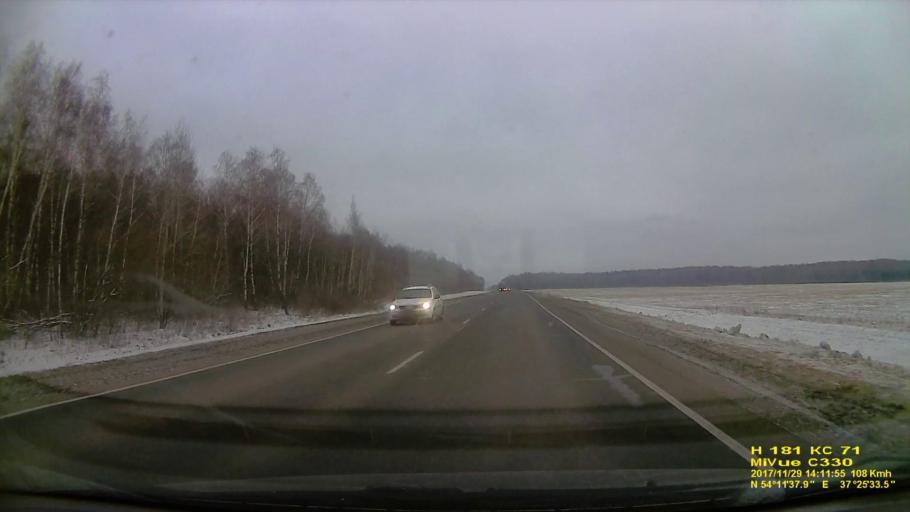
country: RU
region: Tula
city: Barsuki
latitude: 54.1940
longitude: 37.4268
